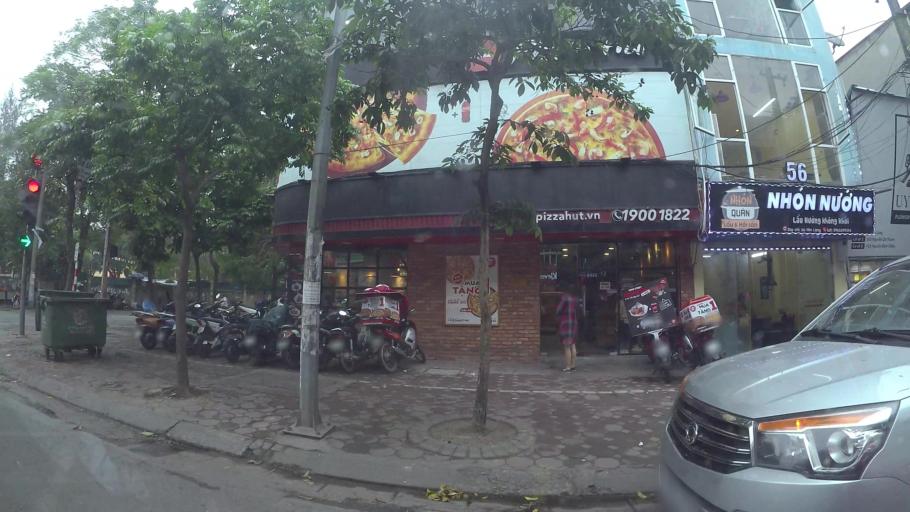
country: VN
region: Ha Noi
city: Dong Da
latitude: 21.0123
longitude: 105.8172
